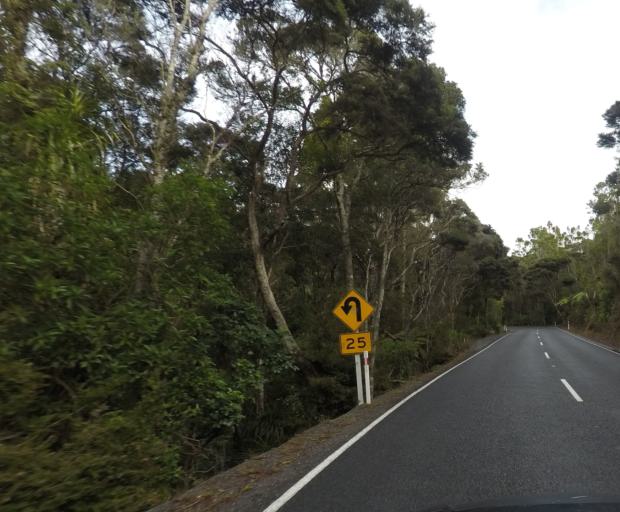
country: NZ
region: Northland
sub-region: Whangarei
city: Ruakaka
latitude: -36.0598
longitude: 174.5693
